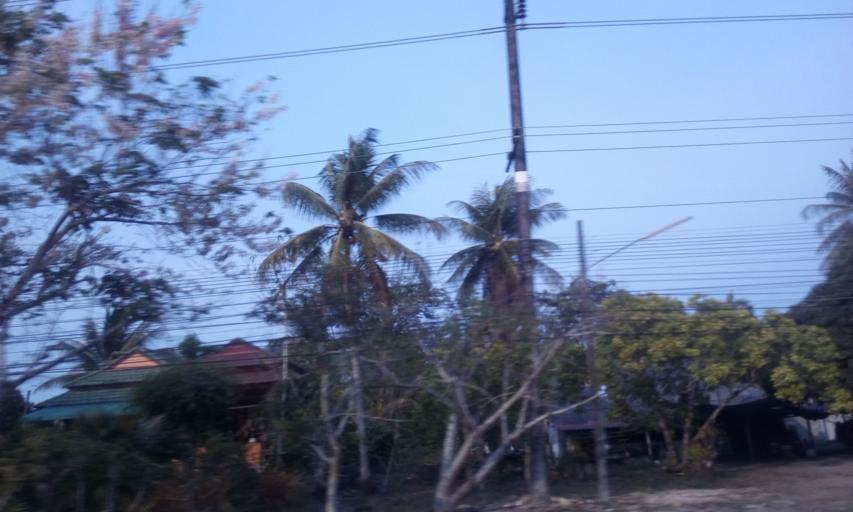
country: TH
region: Chanthaburi
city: Khlung
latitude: 12.4253
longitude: 102.3195
